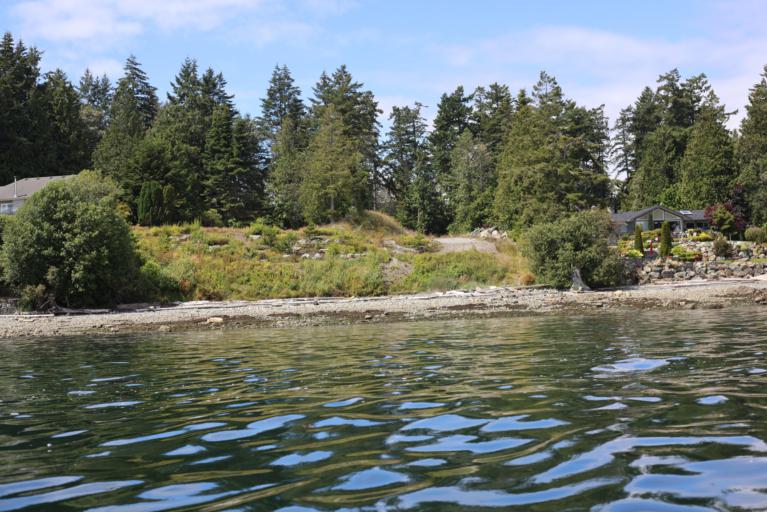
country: CA
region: British Columbia
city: North Saanich
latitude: 48.6080
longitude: -123.3935
